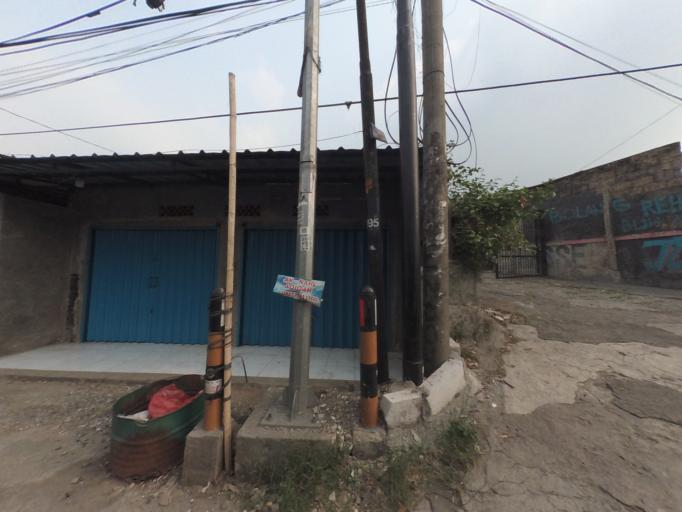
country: ID
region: West Java
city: Ciampea
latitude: -6.5662
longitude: 106.6735
